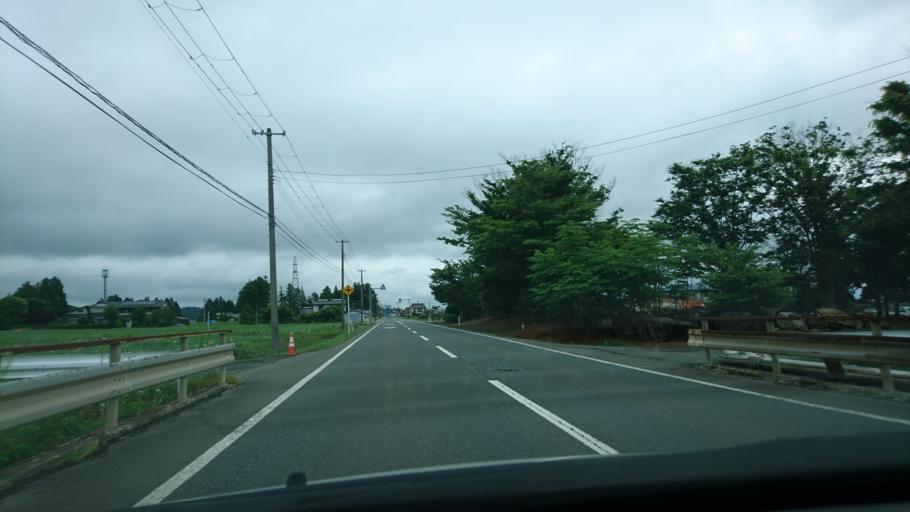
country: JP
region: Iwate
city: Mizusawa
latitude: 39.1254
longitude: 141.0530
